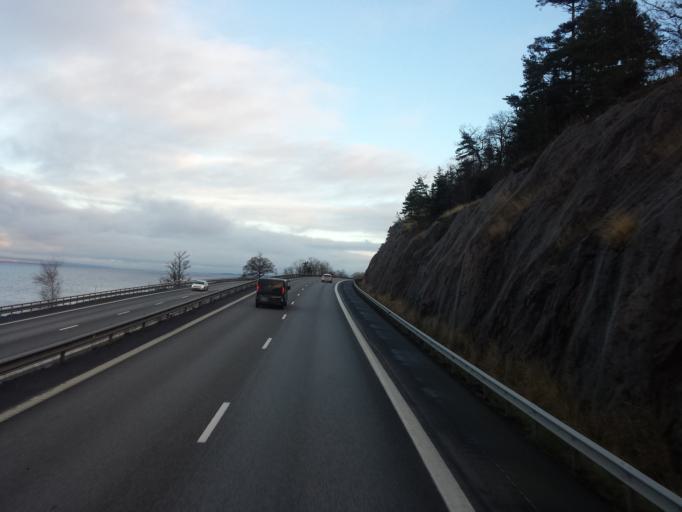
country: SE
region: Joenkoeping
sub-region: Jonkopings Kommun
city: Kaxholmen
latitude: 57.8682
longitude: 14.2712
